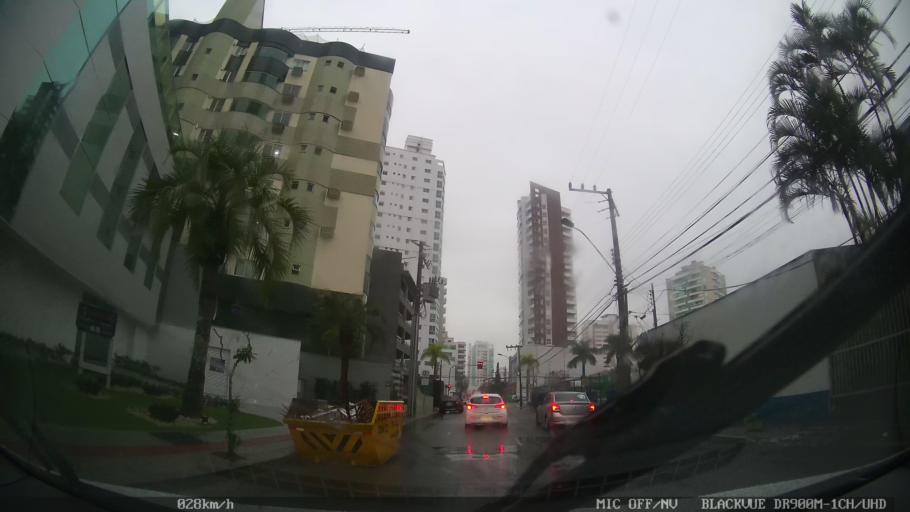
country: BR
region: Santa Catarina
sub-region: Itajai
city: Itajai
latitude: -26.9107
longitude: -48.6566
